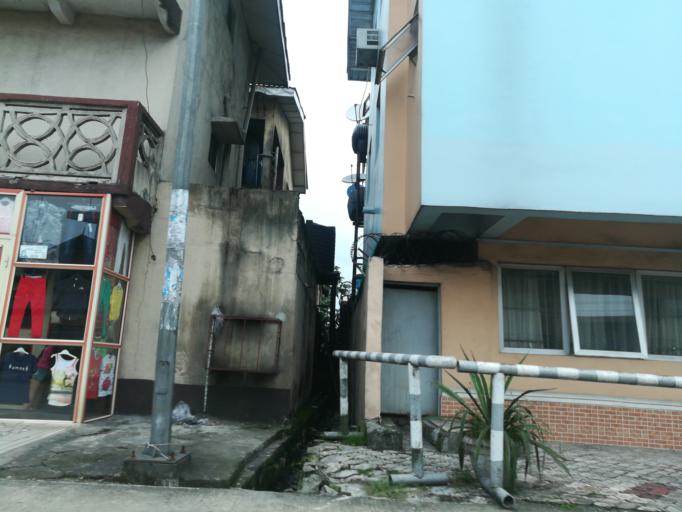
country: NG
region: Rivers
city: Port Harcourt
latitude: 4.7626
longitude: 7.0208
